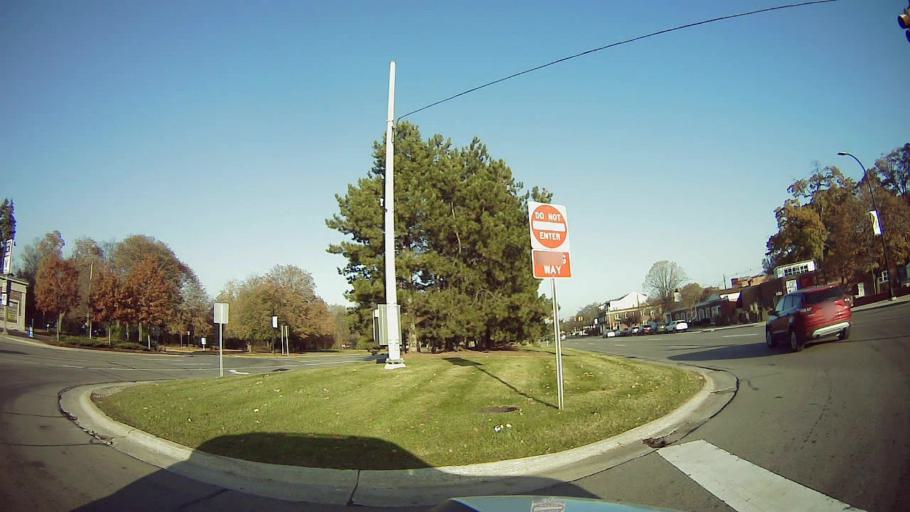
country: US
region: Michigan
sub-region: Oakland County
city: Pleasant Ridge
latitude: 42.4693
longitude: -83.1405
